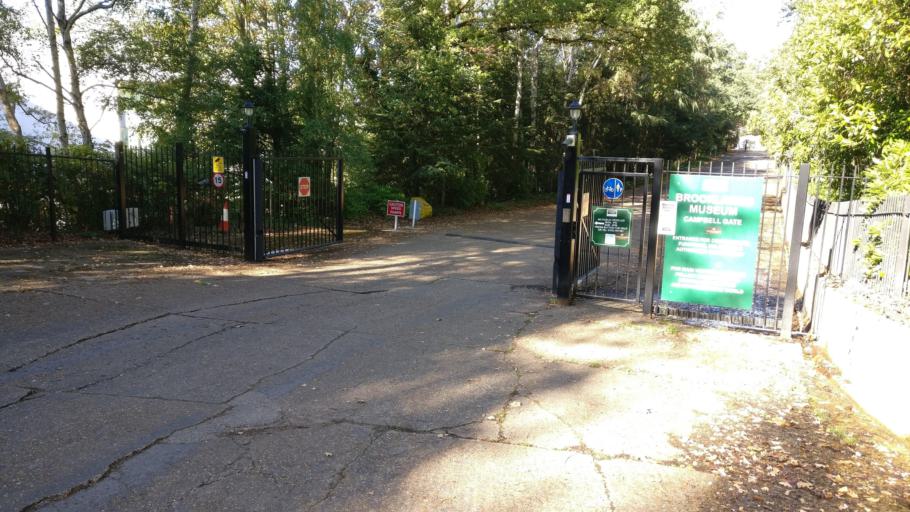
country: GB
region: England
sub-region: Surrey
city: Byfleet
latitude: 51.3532
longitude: -0.4610
